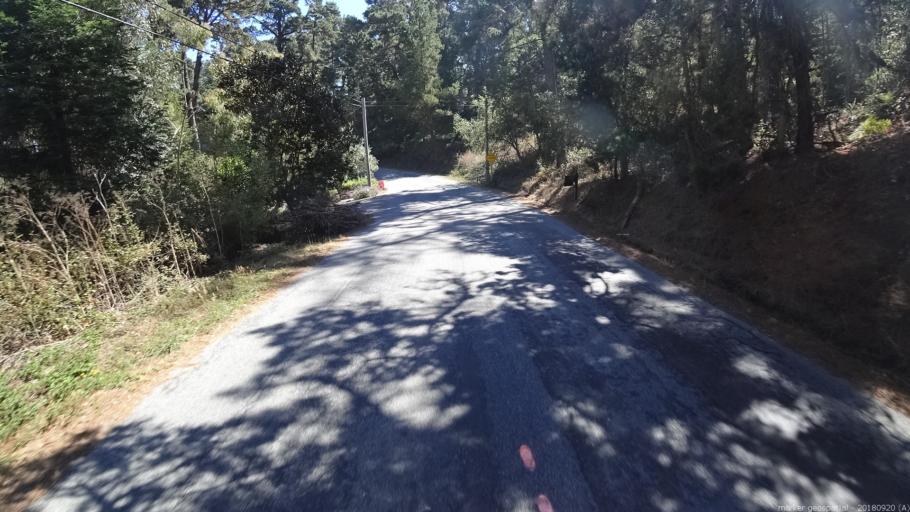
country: US
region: California
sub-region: Monterey County
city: Carmel-by-the-Sea
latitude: 36.5708
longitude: -121.9039
